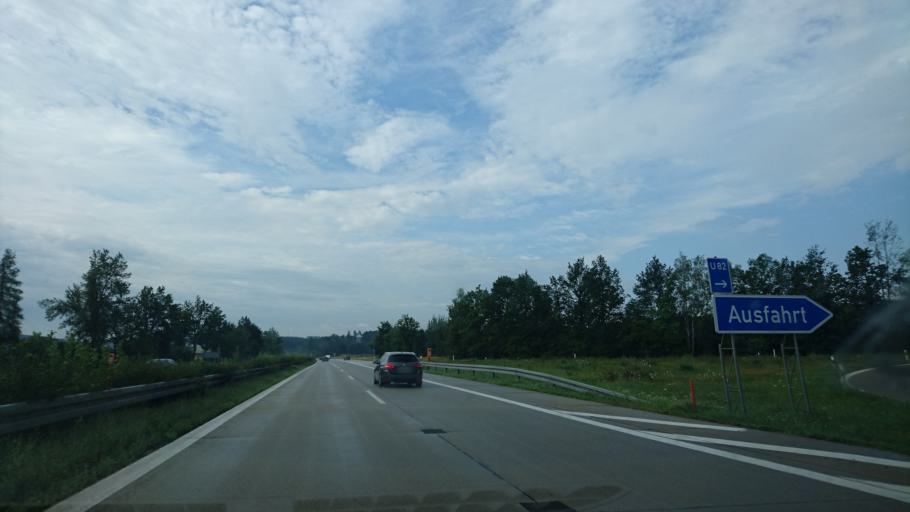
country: DE
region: Bavaria
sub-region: Lower Bavaria
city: Bad Abbach
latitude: 48.9334
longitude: 12.0895
